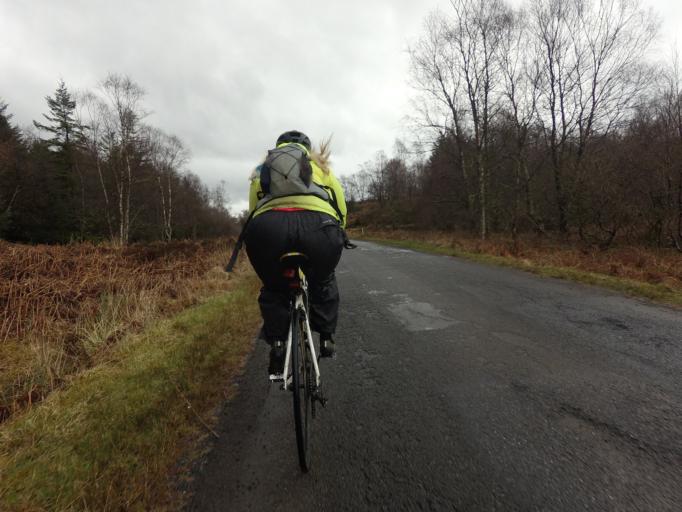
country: GB
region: Scotland
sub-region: West Dunbartonshire
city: Balloch
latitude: 56.2002
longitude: -4.5274
